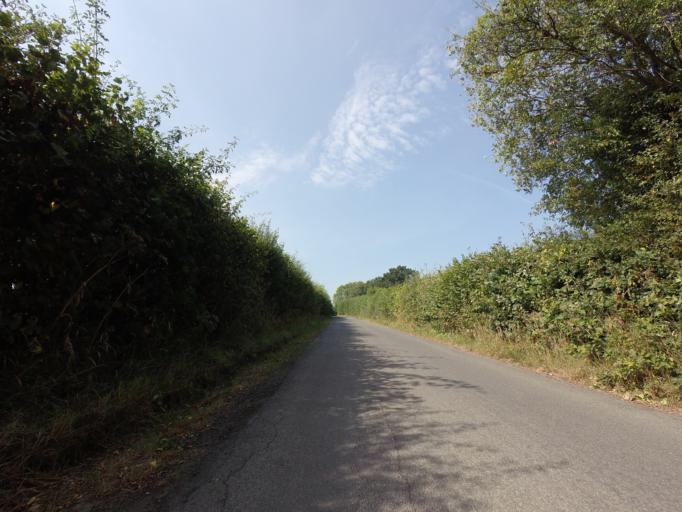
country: GB
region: England
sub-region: Kent
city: Headcorn
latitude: 51.1214
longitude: 0.5938
